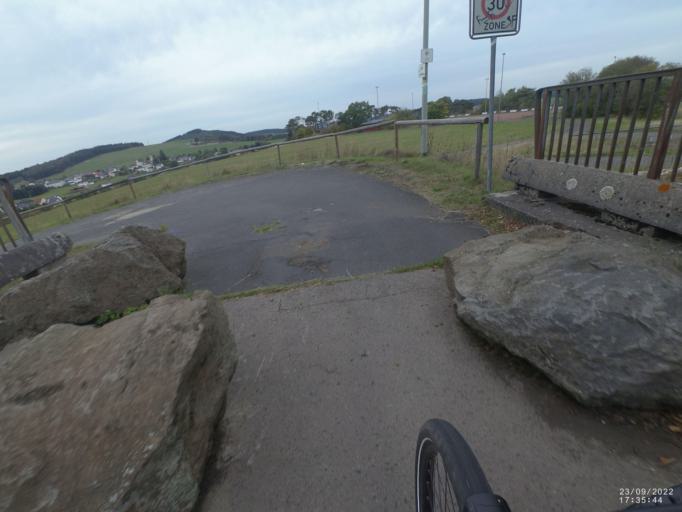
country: DE
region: Rheinland-Pfalz
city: Dockweiler
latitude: 50.2492
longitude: 6.7902
